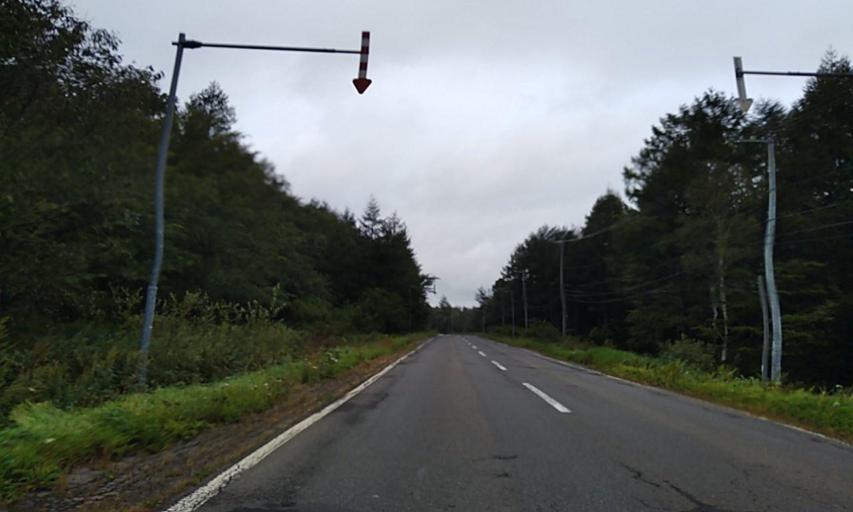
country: JP
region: Hokkaido
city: Kushiro
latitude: 43.4812
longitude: 144.5101
